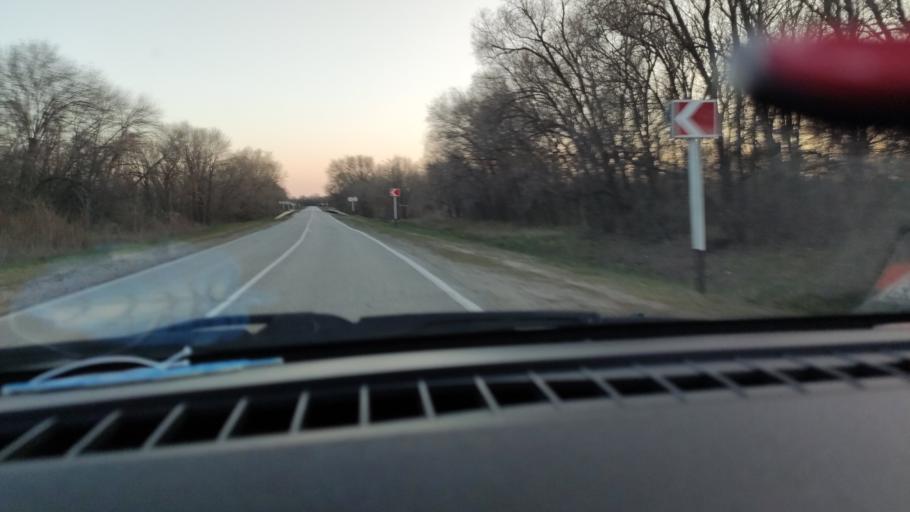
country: RU
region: Saratov
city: Privolzhskiy
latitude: 51.2745
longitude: 45.9488
